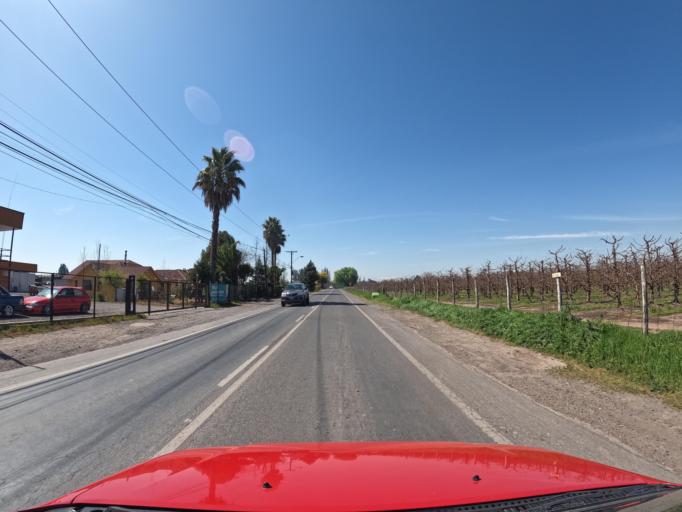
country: CL
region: Maule
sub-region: Provincia de Curico
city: Rauco
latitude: -34.9956
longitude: -71.3576
